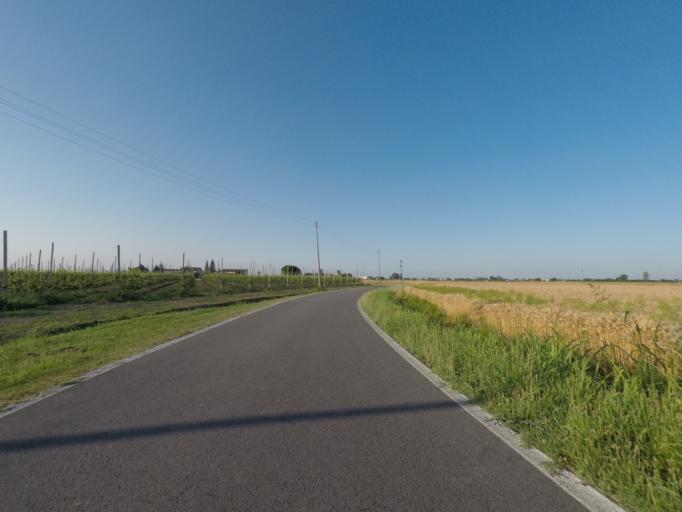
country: IT
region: Veneto
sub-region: Provincia di Rovigo
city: Villamarzana
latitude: 45.0283
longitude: 11.6761
